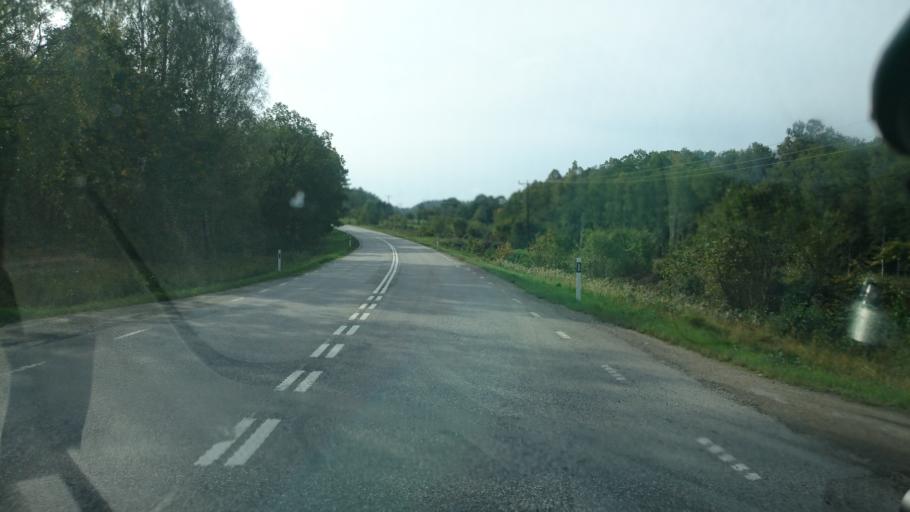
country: SE
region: Vaestra Goetaland
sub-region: Alingsas Kommun
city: Sollebrunn
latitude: 58.0590
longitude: 12.4664
